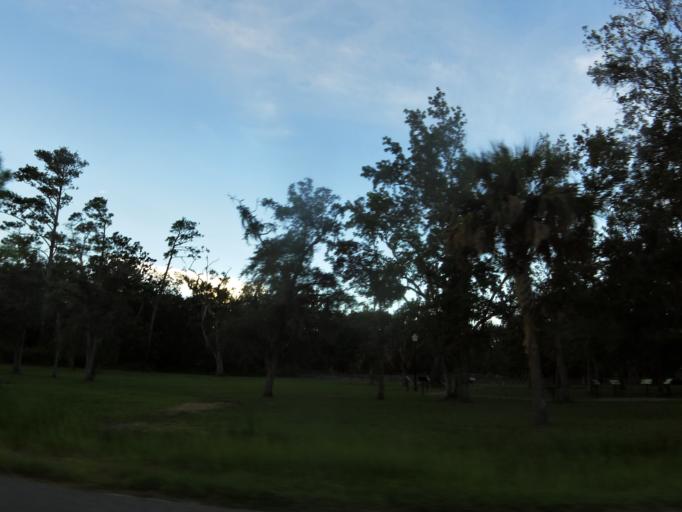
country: US
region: Georgia
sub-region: Camden County
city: St. Marys
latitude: 30.7214
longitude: -81.5543
